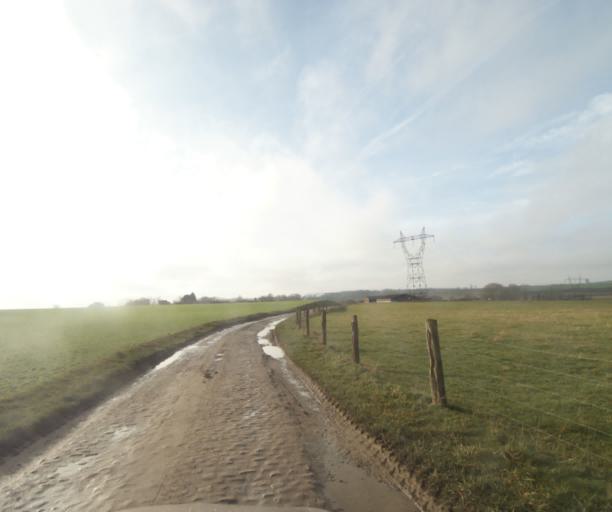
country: FR
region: Nord-Pas-de-Calais
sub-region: Departement du Nord
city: Thiant
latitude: 50.2939
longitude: 3.4607
